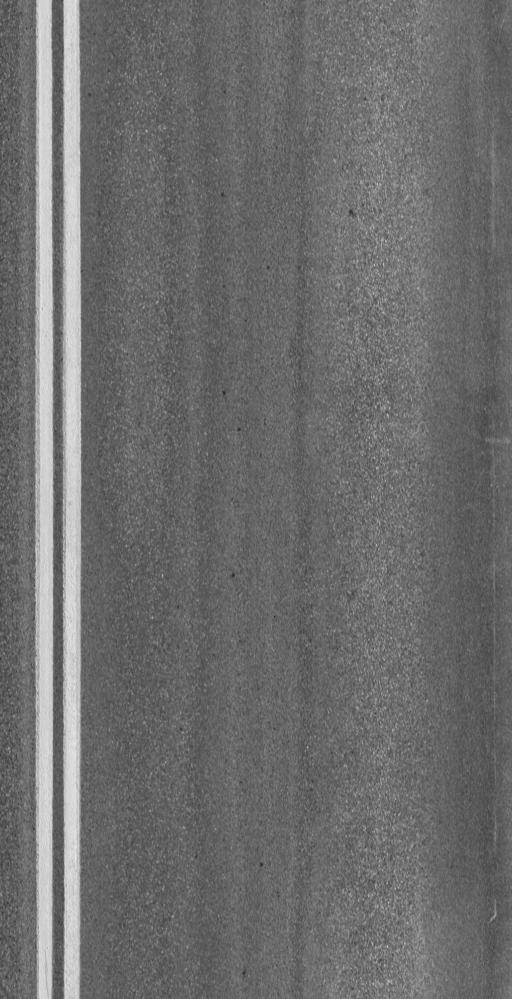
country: US
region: Vermont
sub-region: Chittenden County
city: Hinesburg
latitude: 44.3431
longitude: -73.1104
